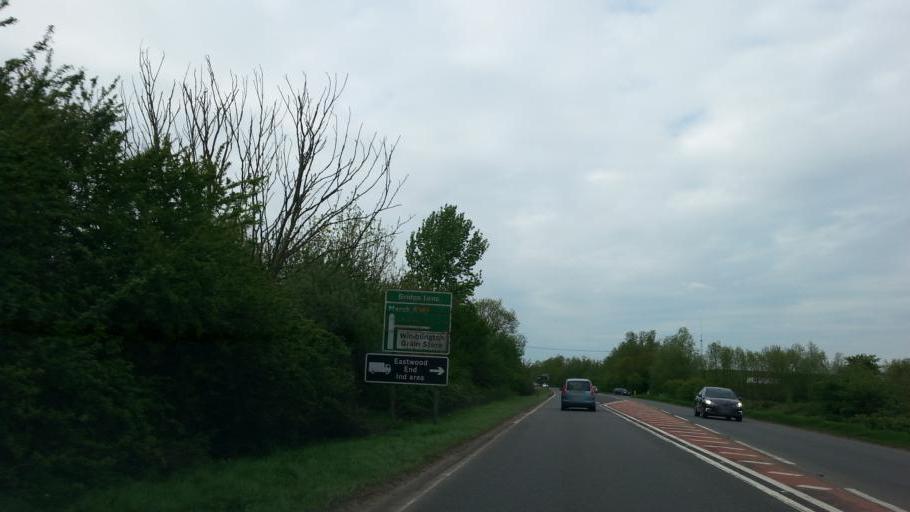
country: GB
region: England
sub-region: Cambridgeshire
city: Doddington
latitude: 52.5155
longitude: 0.0904
